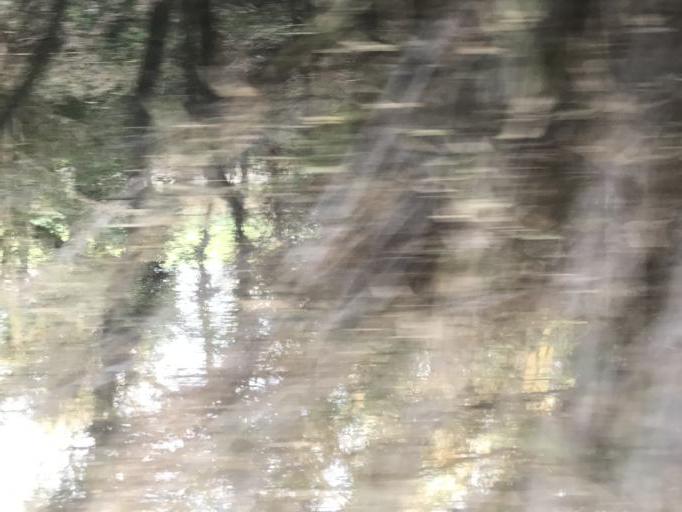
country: AR
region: Cordoba
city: Leones
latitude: -32.6816
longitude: -62.2048
